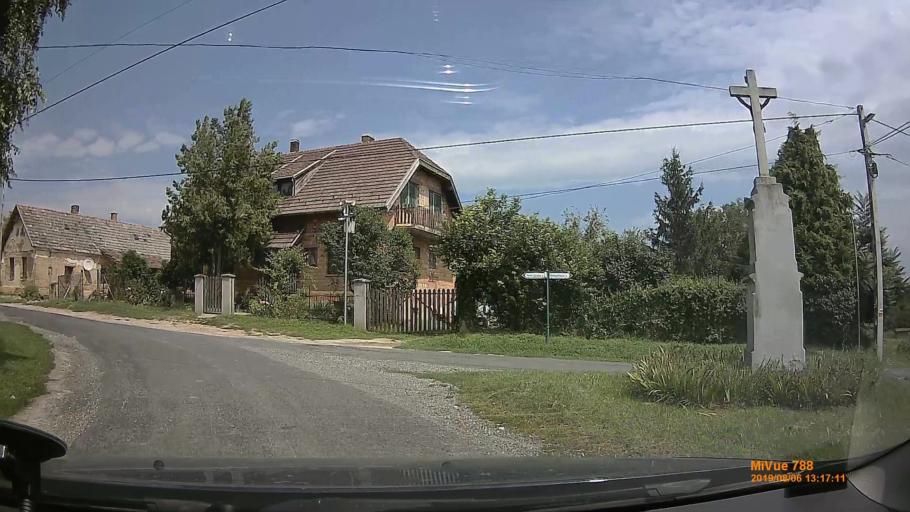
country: HU
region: Zala
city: Pacsa
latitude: 46.6261
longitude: 17.0623
